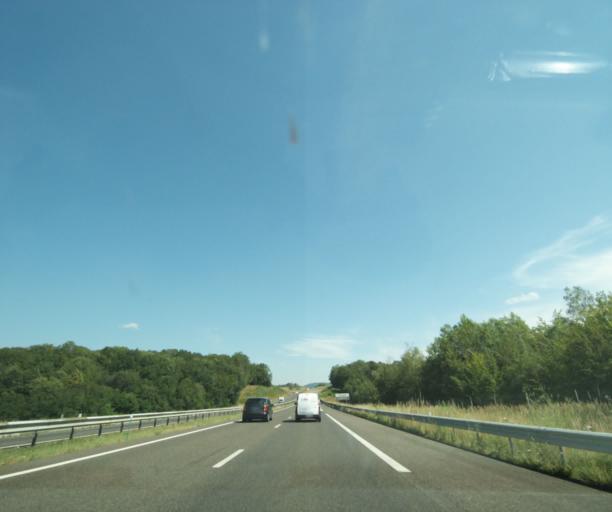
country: FR
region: Lorraine
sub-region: Departement de Meurthe-et-Moselle
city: Dommartin-les-Toul
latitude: 48.6448
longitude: 5.8804
